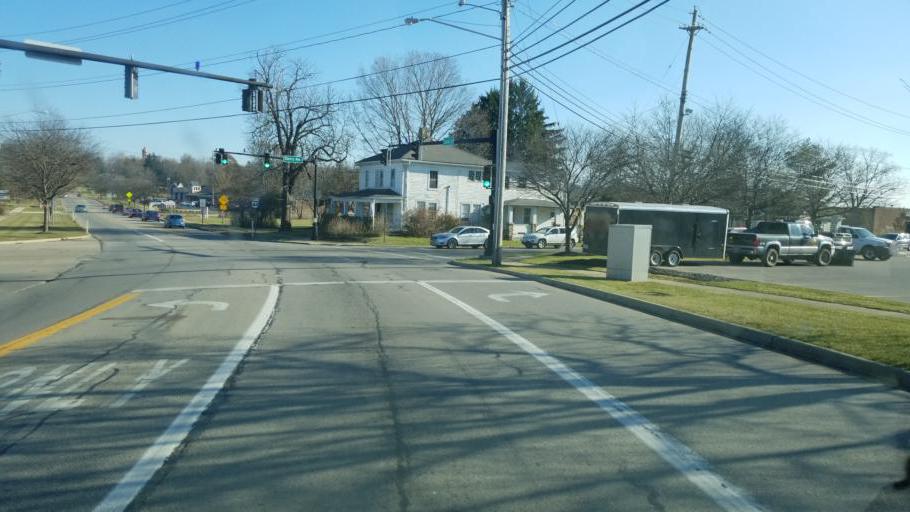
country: US
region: Ohio
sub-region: Geauga County
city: Chardon
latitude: 41.5834
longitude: -81.2132
